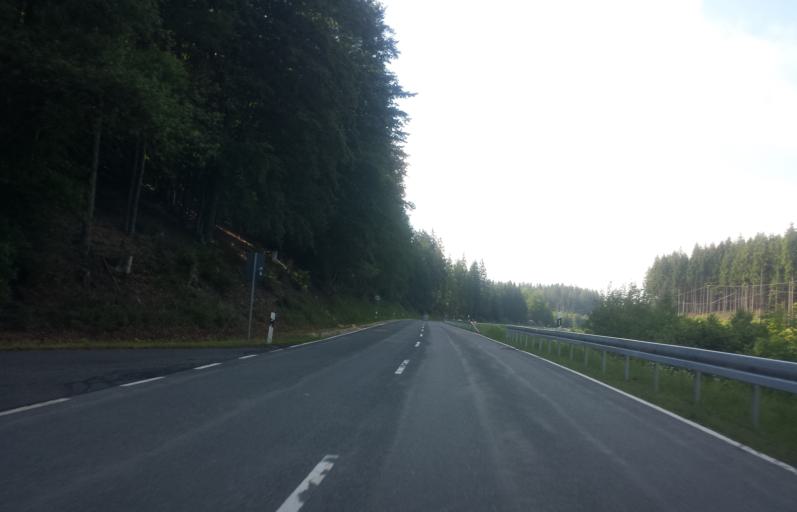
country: DE
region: Bavaria
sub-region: Upper Franconia
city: Ludwigsstadt
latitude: 50.4584
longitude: 11.3751
